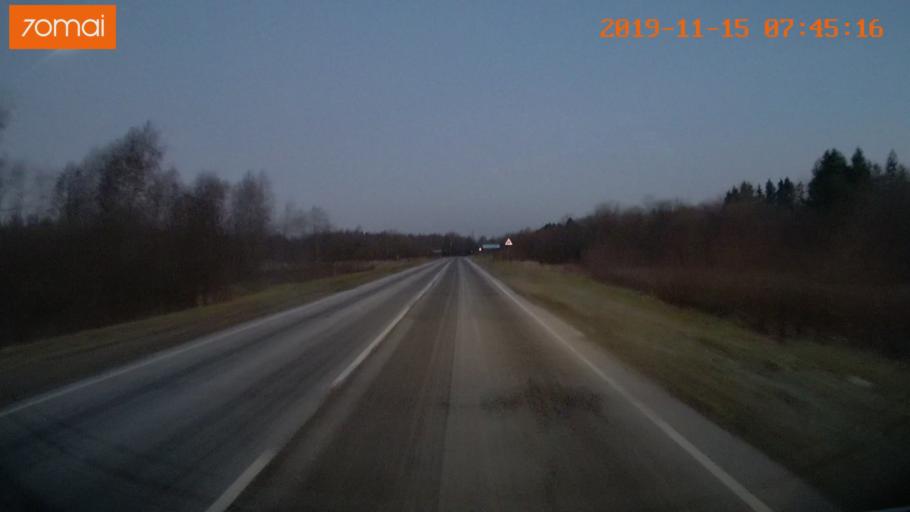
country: RU
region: Vologda
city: Sheksna
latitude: 58.8223
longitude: 38.3003
